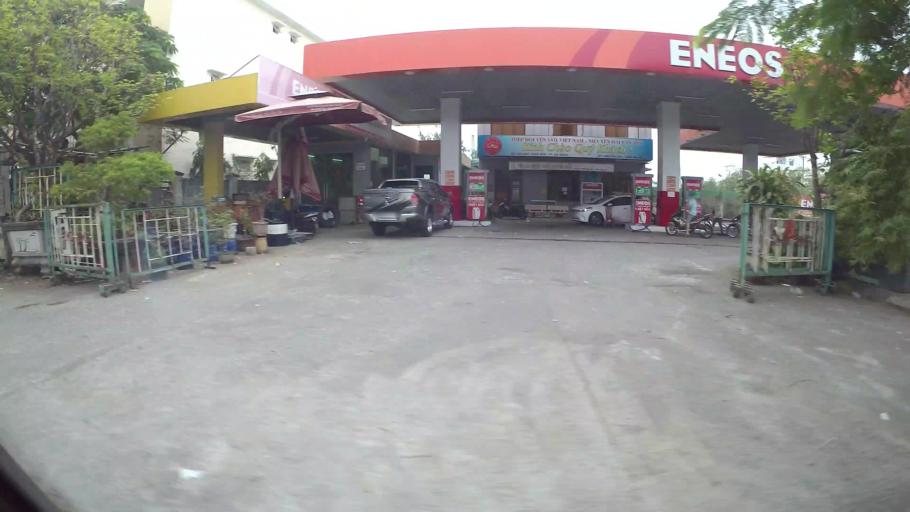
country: VN
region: Da Nang
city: Son Tra
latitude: 16.0453
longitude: 108.2398
